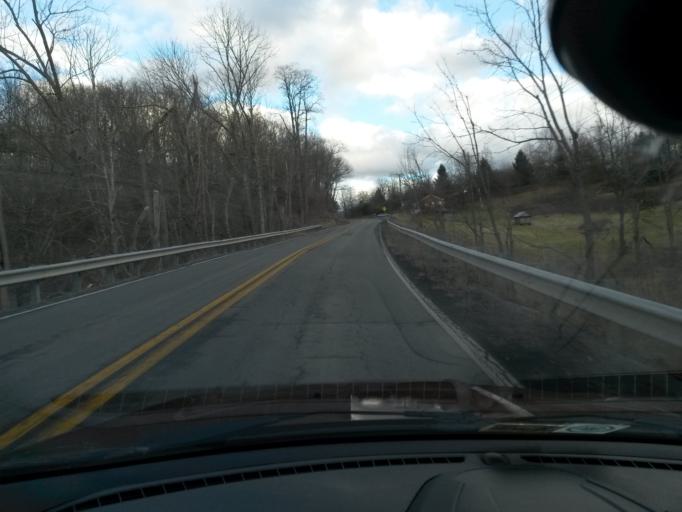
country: US
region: West Virginia
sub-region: Monroe County
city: Union
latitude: 37.5889
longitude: -80.5191
